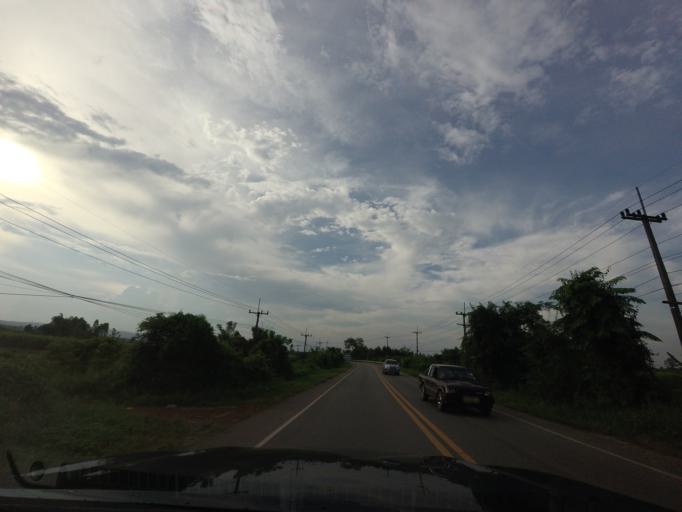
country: TH
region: Changwat Udon Thani
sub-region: Amphoe Ban Phue
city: Ban Phue
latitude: 17.7139
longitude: 102.4121
